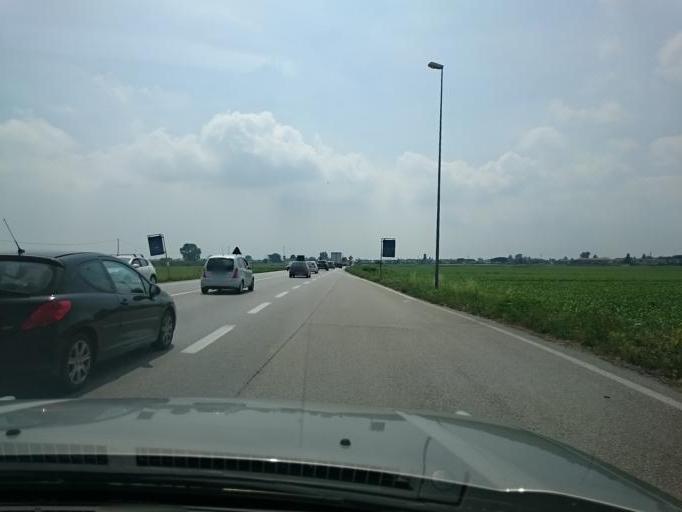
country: IT
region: Veneto
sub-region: Provincia di Padova
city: Codevigo
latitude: 45.2532
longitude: 12.1319
